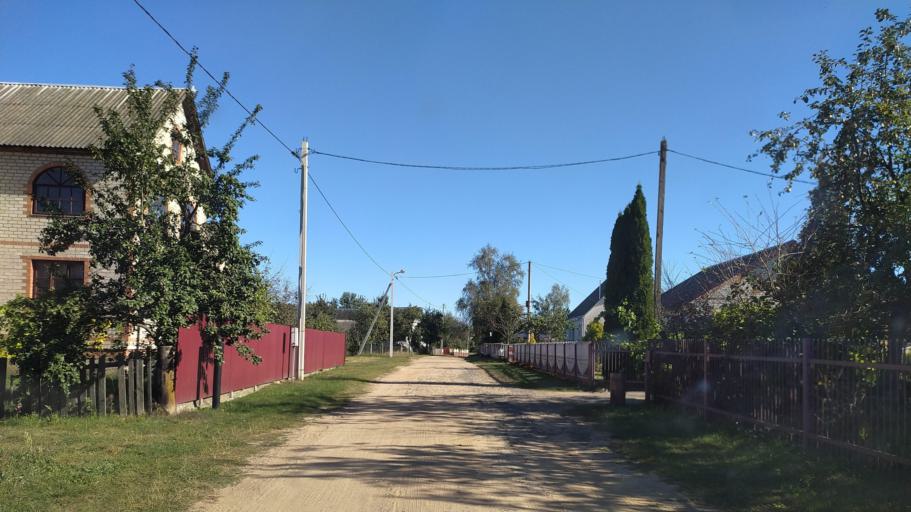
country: BY
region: Brest
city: Pruzhany
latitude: 52.4839
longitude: 24.7088
